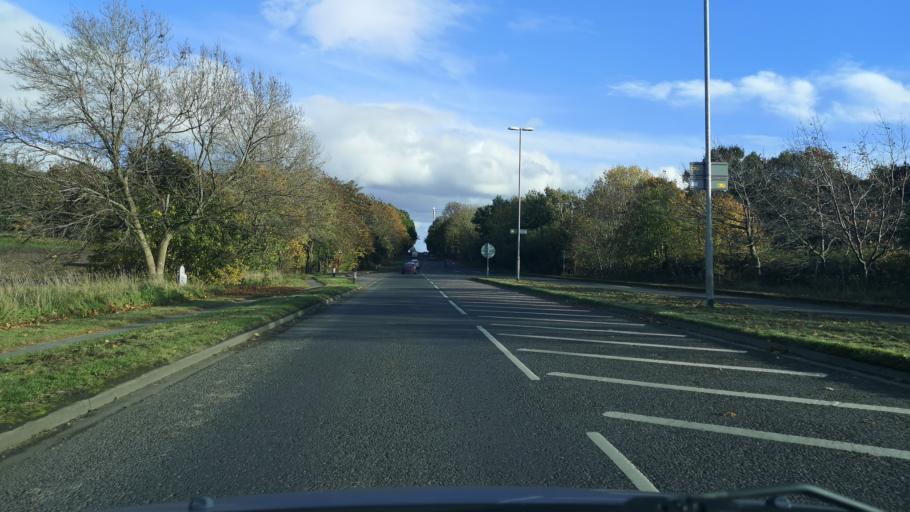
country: GB
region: England
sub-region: City and Borough of Wakefield
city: Middlestown
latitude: 53.6240
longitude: -1.5776
